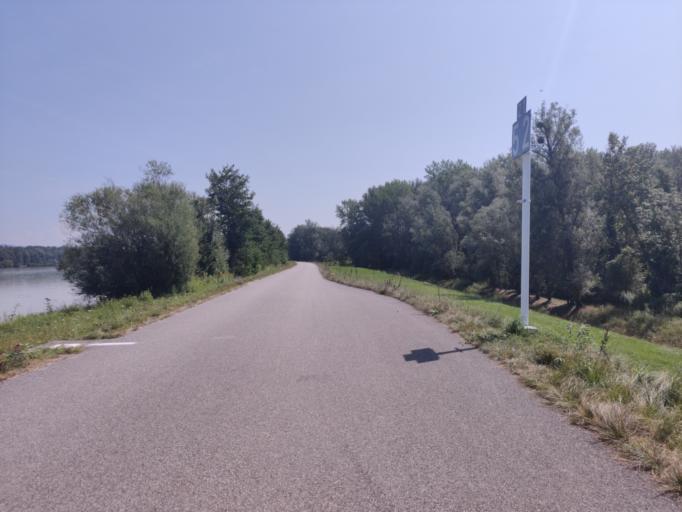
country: AT
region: Upper Austria
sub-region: Politischer Bezirk Urfahr-Umgebung
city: Goldworth
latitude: 48.3149
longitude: 14.0851
